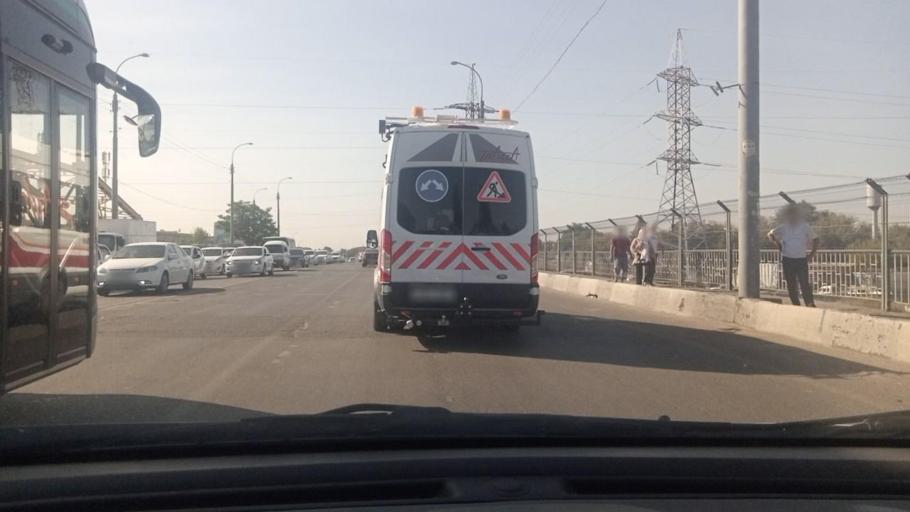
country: UZ
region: Toshkent Shahri
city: Bektemir
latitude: 41.2356
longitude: 69.3323
